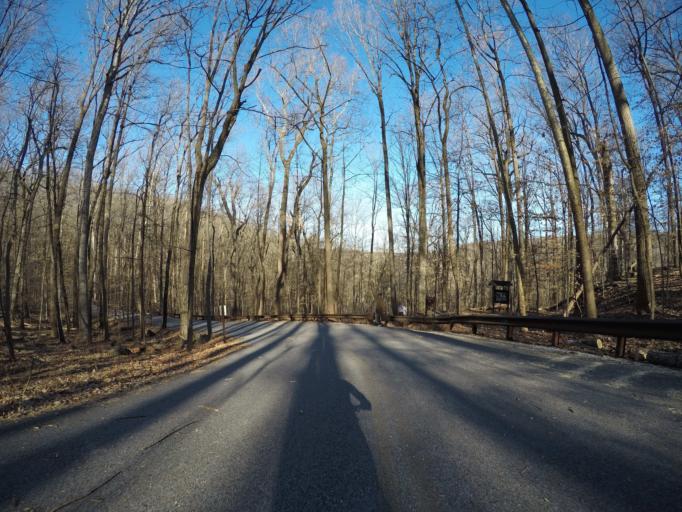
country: US
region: Maryland
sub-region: Howard County
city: Ellicott City
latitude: 39.2914
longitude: -76.7876
